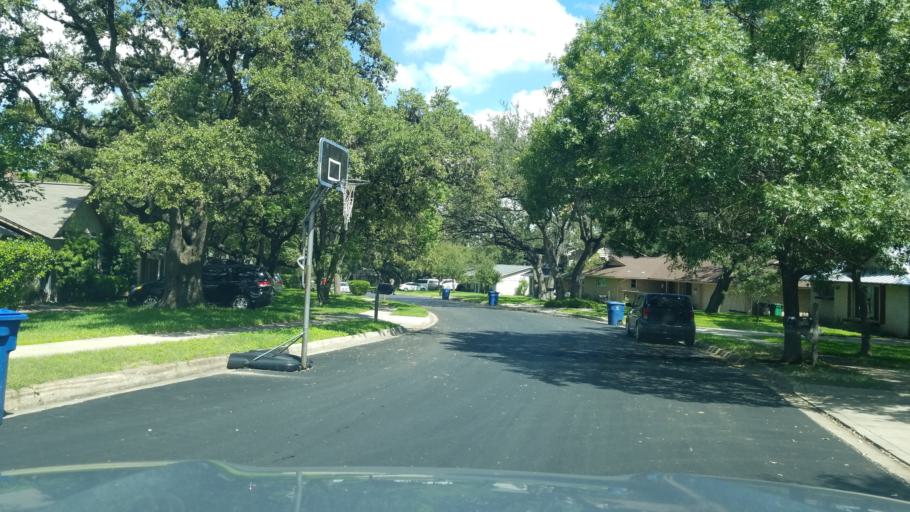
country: US
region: Texas
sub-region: Bexar County
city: Castle Hills
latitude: 29.5464
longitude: -98.5025
